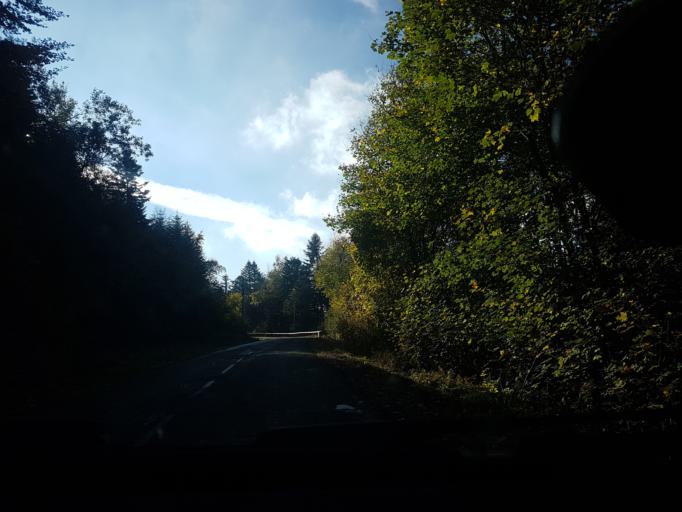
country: FR
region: Franche-Comte
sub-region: Departement de la Haute-Saone
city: Plancher-les-Mines
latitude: 47.7729
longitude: 6.7712
